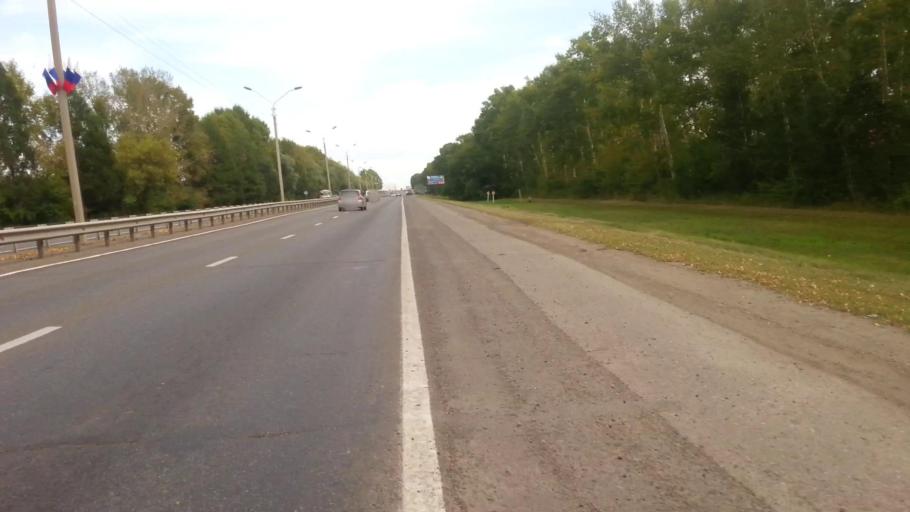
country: RU
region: Altai Krai
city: Vlasikha
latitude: 53.3525
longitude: 83.5701
